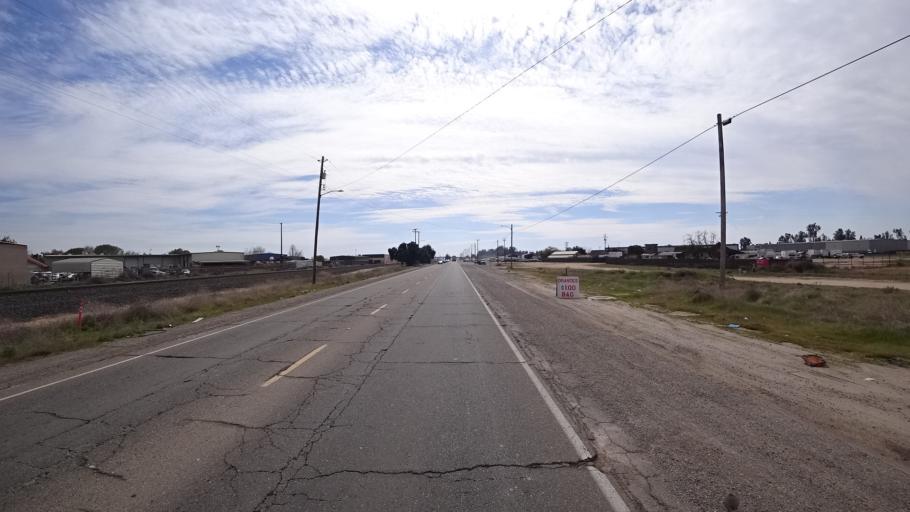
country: US
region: California
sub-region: Fresno County
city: West Park
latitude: 36.8036
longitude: -119.8726
